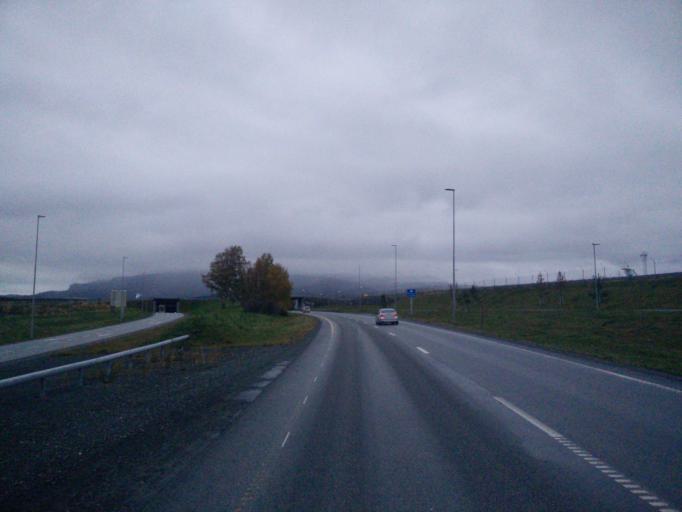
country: NO
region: Nord-Trondelag
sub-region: Stjordal
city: Stjordal
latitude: 63.4531
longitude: 10.9098
